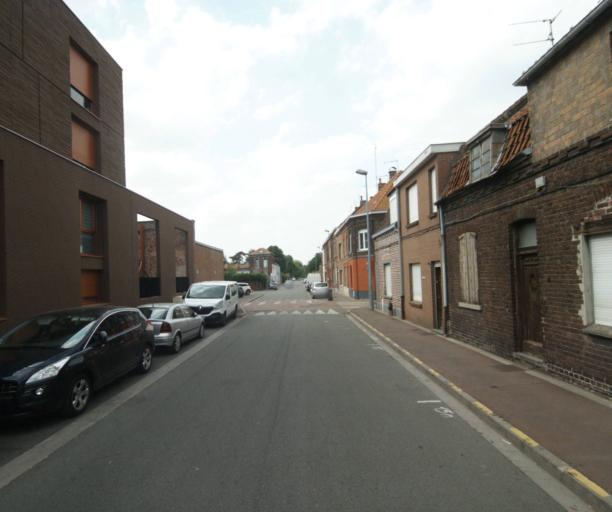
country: FR
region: Nord-Pas-de-Calais
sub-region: Departement du Nord
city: Tourcoing
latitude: 50.7331
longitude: 3.1473
